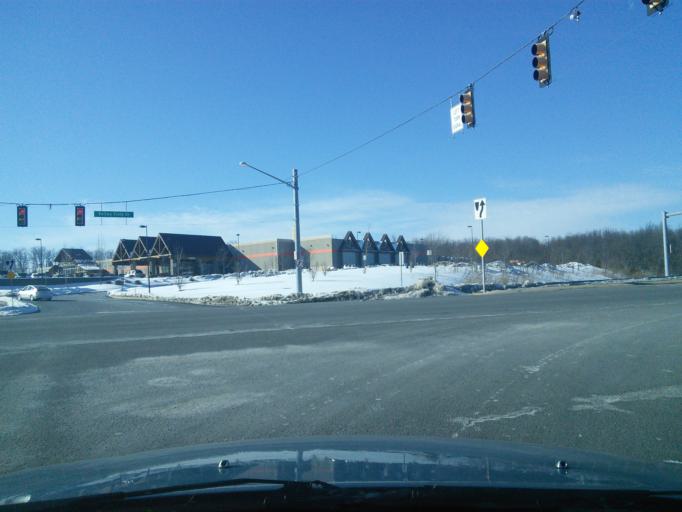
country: US
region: Pennsylvania
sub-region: Centre County
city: Park Forest Village
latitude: 40.8133
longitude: -77.9213
